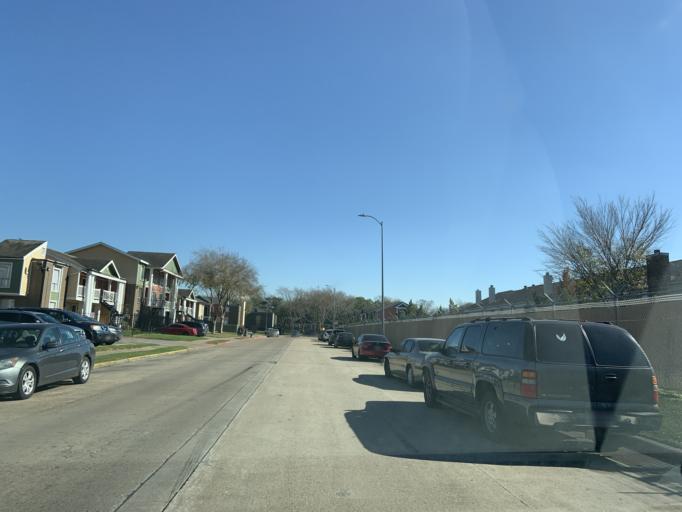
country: US
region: Texas
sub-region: Harris County
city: Bellaire
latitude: 29.6787
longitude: -95.5072
